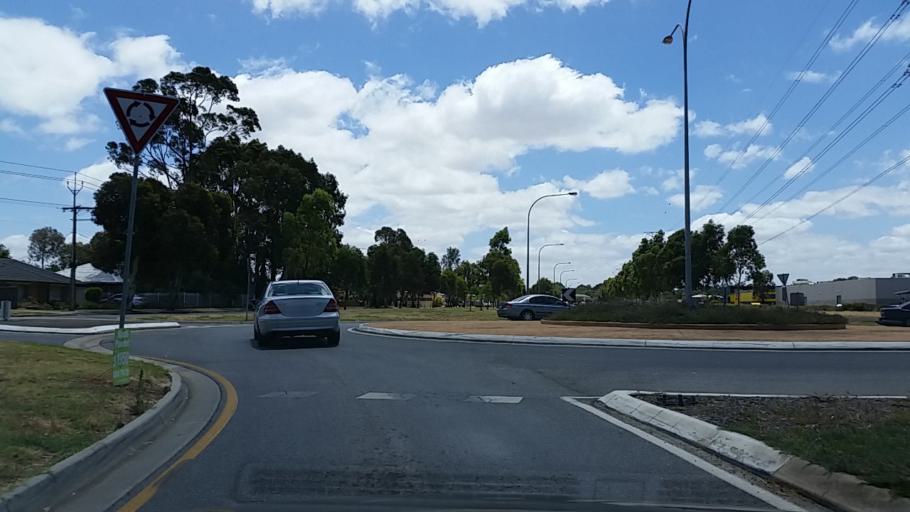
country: AU
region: South Australia
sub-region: Salisbury
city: Salisbury
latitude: -34.7682
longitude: 138.6207
